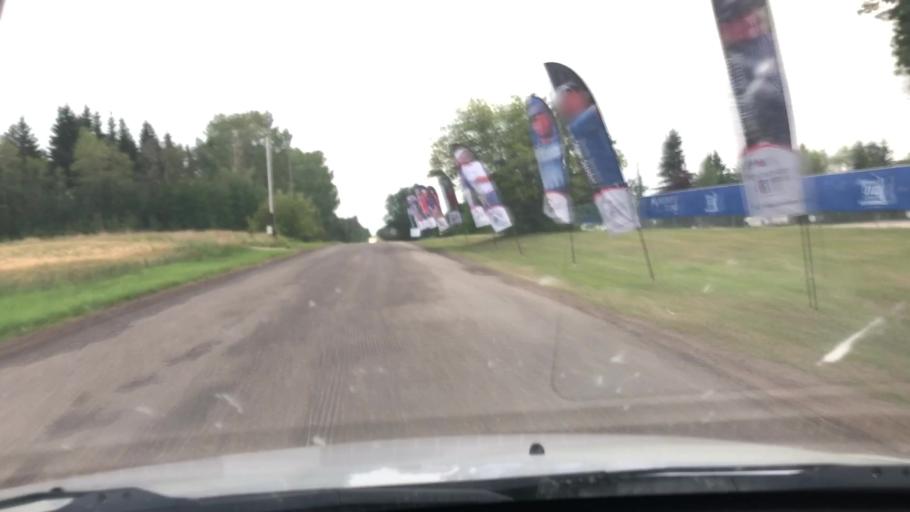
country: CA
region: Alberta
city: Devon
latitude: 53.4186
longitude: -113.6892
